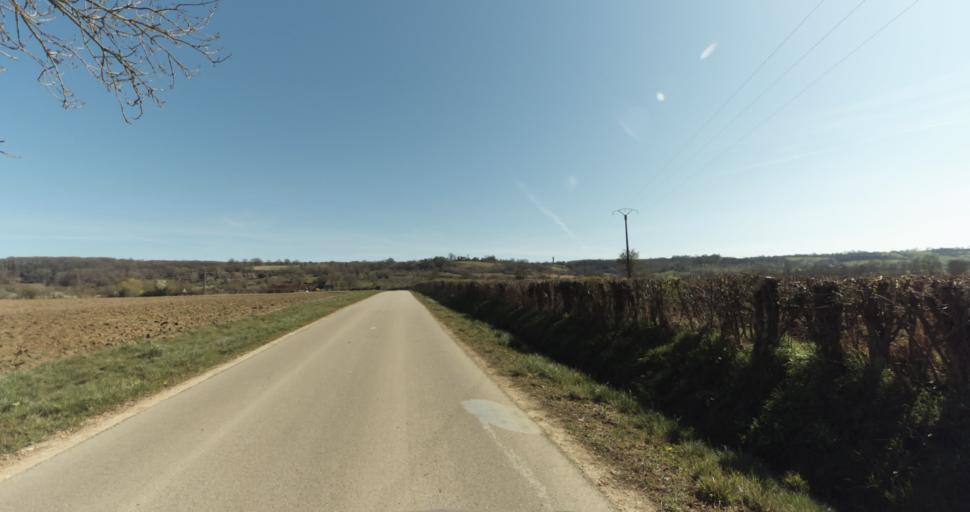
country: FR
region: Lower Normandy
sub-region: Departement du Calvados
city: Saint-Pierre-sur-Dives
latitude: 48.9639
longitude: 0.0551
